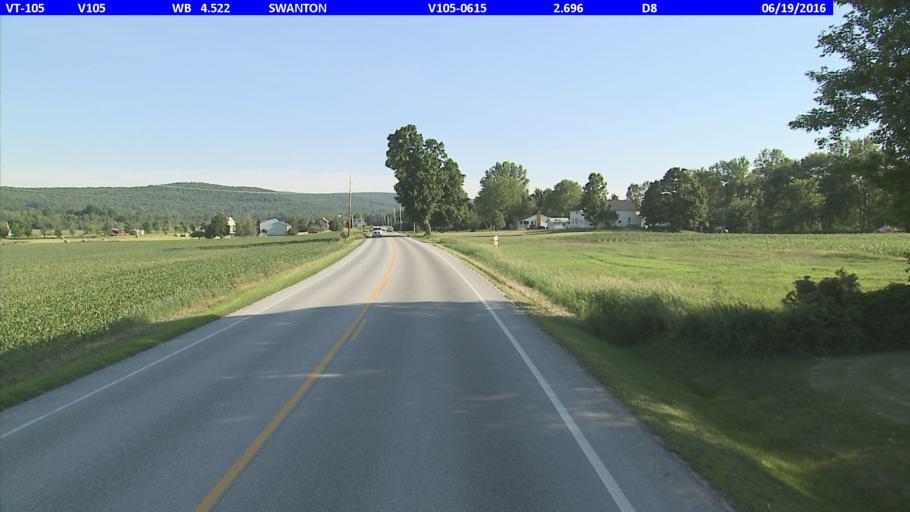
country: US
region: Vermont
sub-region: Franklin County
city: Saint Albans
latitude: 44.8714
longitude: -73.0326
